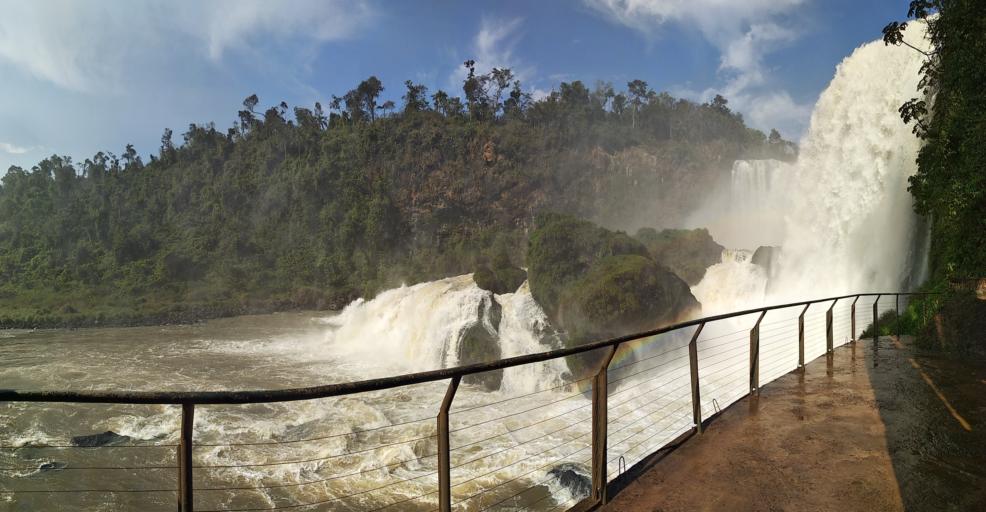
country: PY
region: Alto Parana
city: Presidente Franco
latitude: -25.5618
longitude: -54.6319
